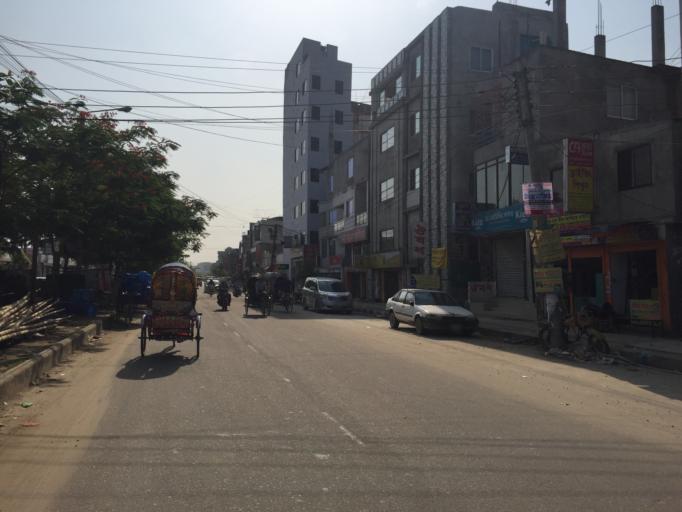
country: BD
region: Dhaka
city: Paltan
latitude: 23.7987
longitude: 90.4321
